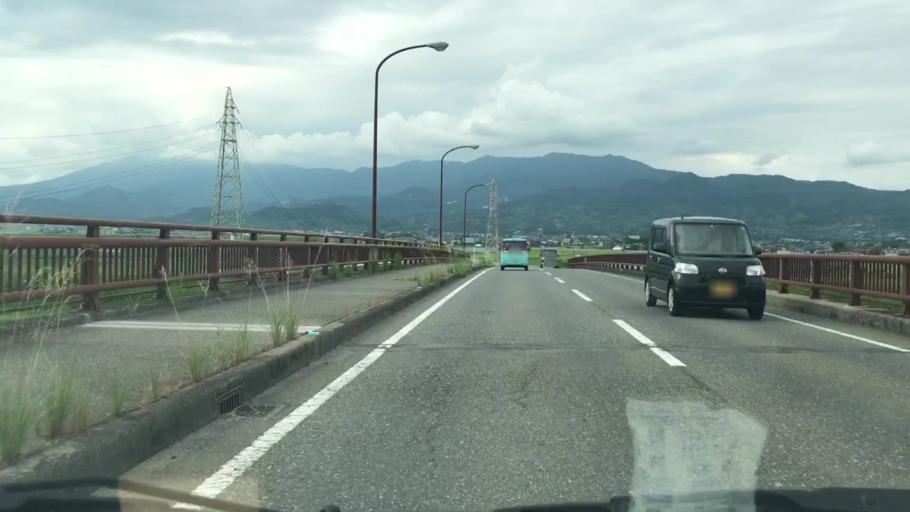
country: JP
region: Saga Prefecture
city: Saga-shi
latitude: 33.2782
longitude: 130.2541
